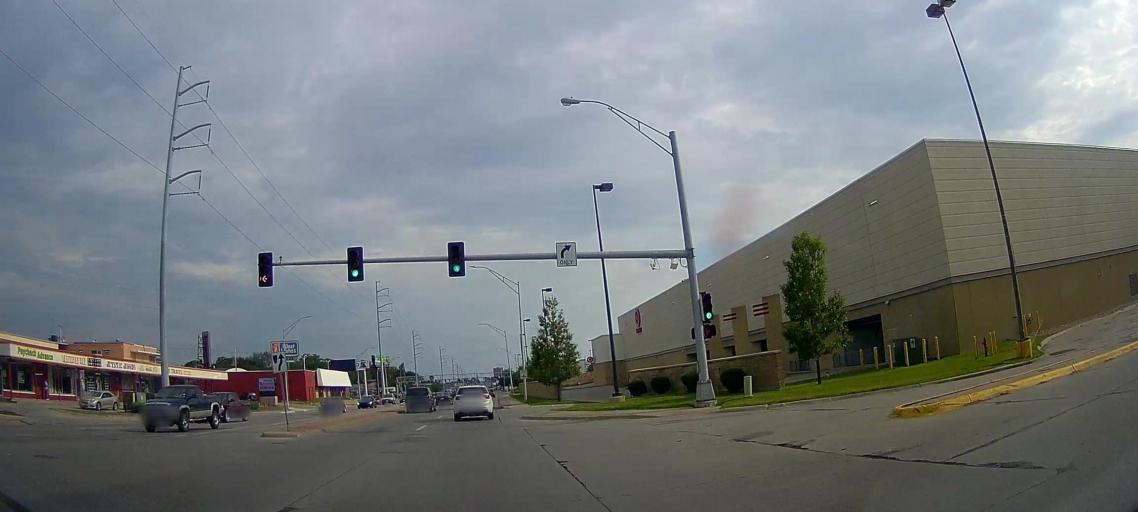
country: US
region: Nebraska
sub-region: Douglas County
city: Ralston
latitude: 41.2619
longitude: -96.0241
